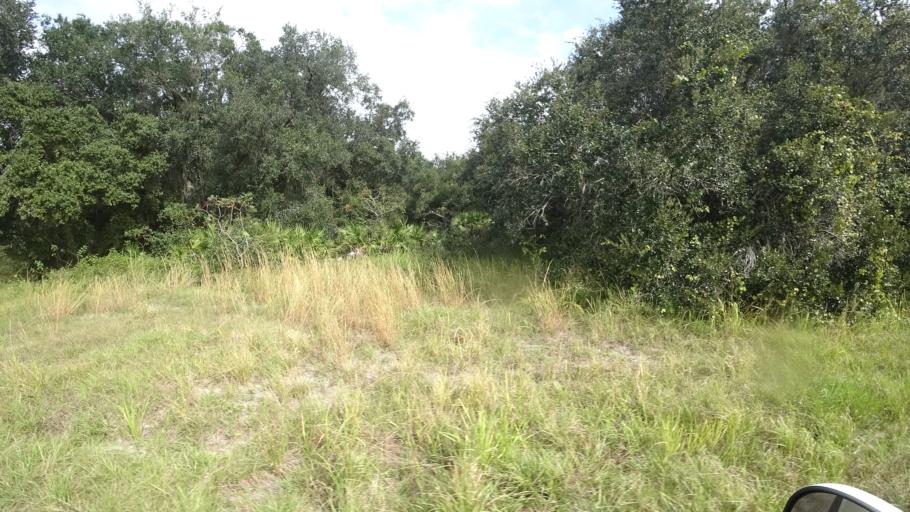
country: US
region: Florida
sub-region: Hillsborough County
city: Wimauma
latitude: 27.5877
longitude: -82.3035
